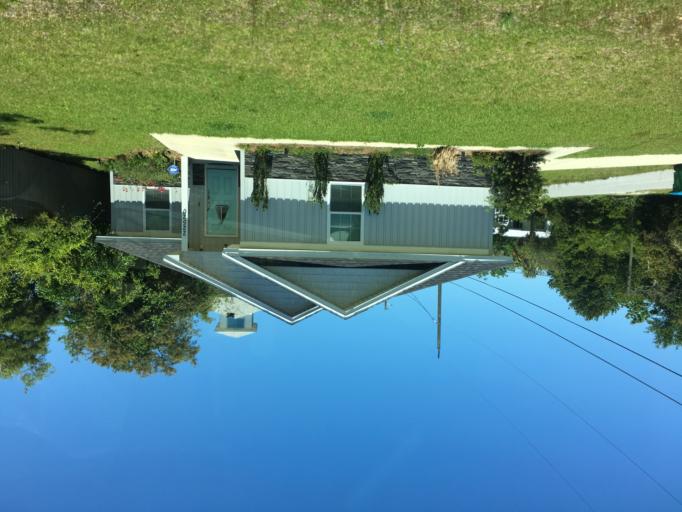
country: US
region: Florida
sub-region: Bay County
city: Laguna Beach
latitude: 30.2621
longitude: -85.9676
